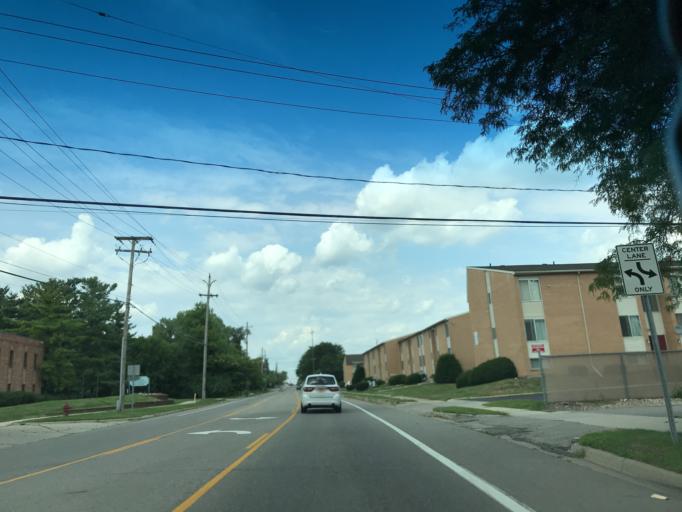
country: US
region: Michigan
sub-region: Washtenaw County
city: Ypsilanti
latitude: 42.2456
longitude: -83.6610
